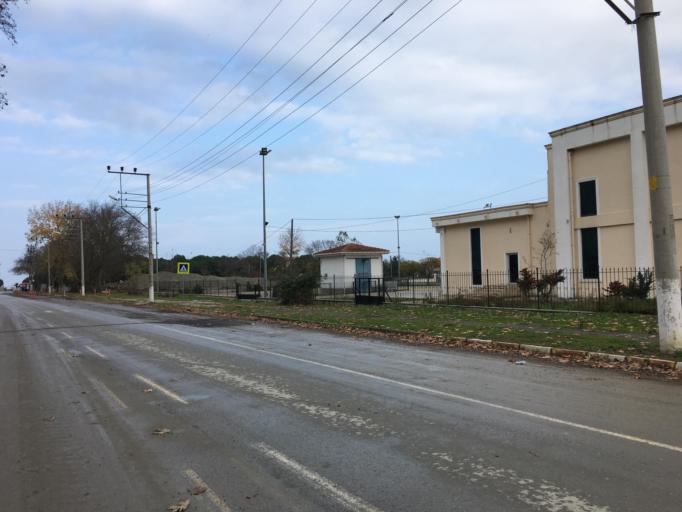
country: TR
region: Samsun
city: Alacam
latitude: 41.6312
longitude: 35.6092
